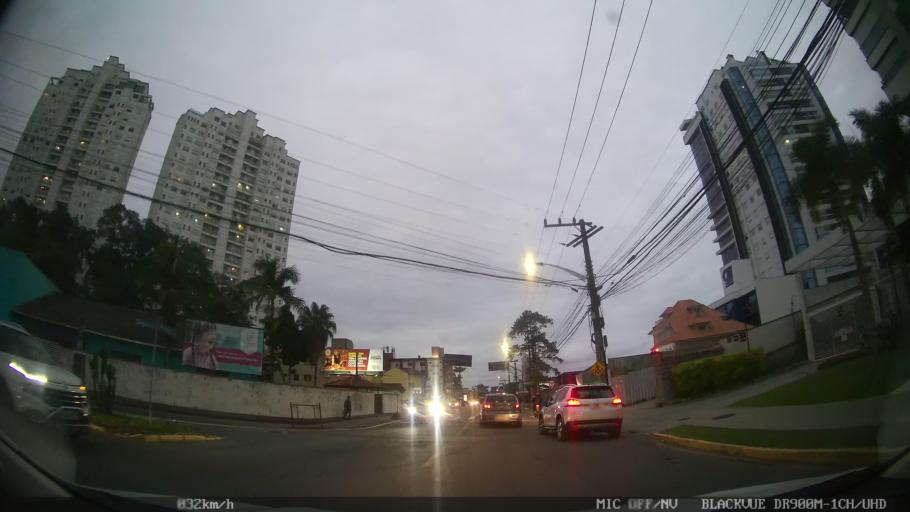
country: BR
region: Santa Catarina
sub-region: Joinville
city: Joinville
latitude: -26.3075
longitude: -48.8477
